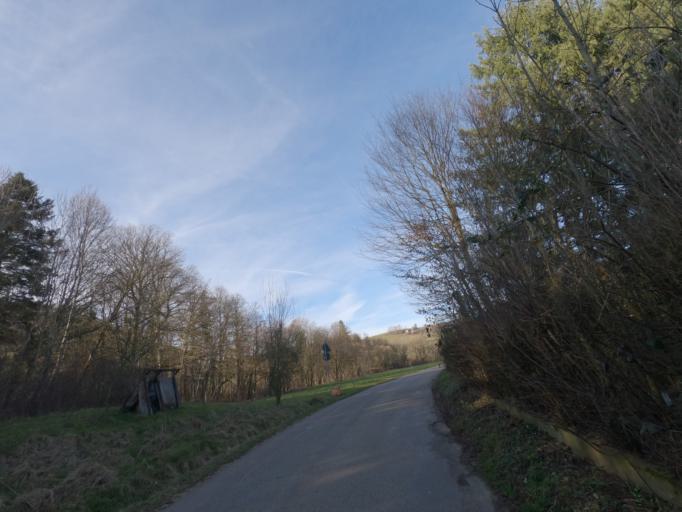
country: DE
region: Baden-Wuerttemberg
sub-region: Regierungsbezirk Stuttgart
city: Ottenbach
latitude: 48.7220
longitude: 9.7877
